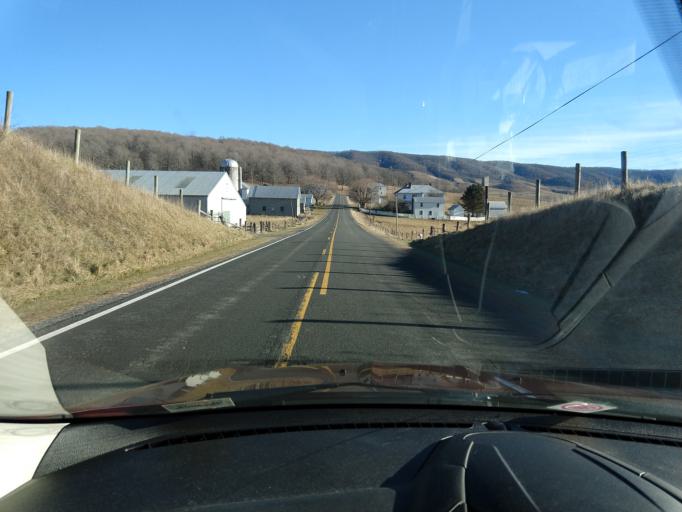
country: US
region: Virginia
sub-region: Highland County
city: Monterey
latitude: 38.4331
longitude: -79.6352
